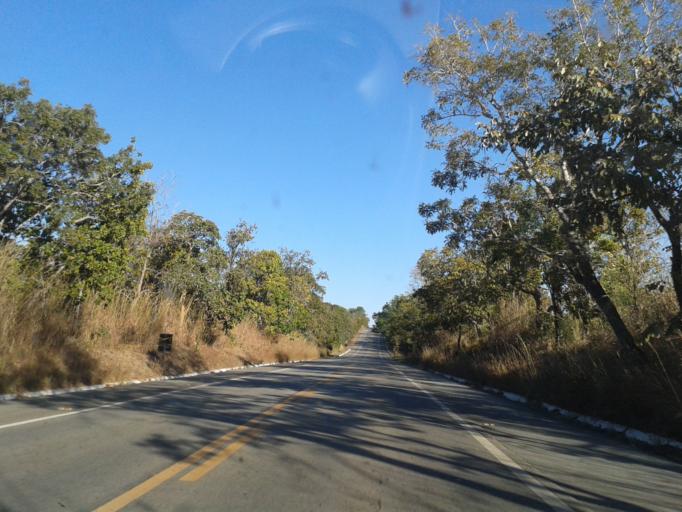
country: BR
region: Goias
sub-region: Itapuranga
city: Itapuranga
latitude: -15.5329
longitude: -50.2930
